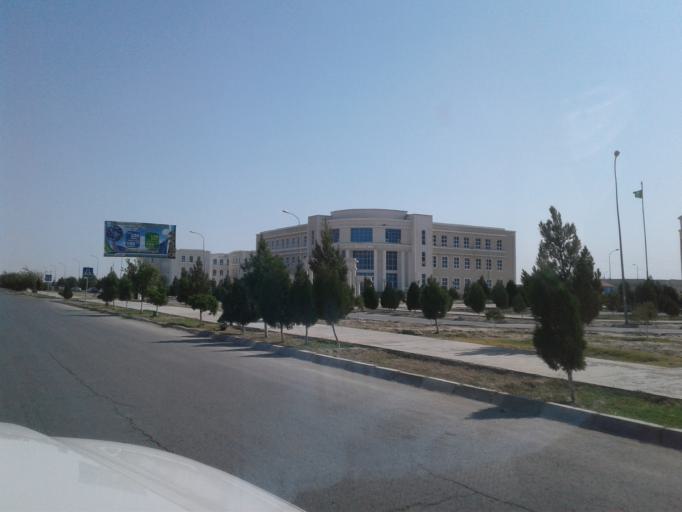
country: TM
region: Balkan
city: Gazanjyk
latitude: 39.2580
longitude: 55.5385
